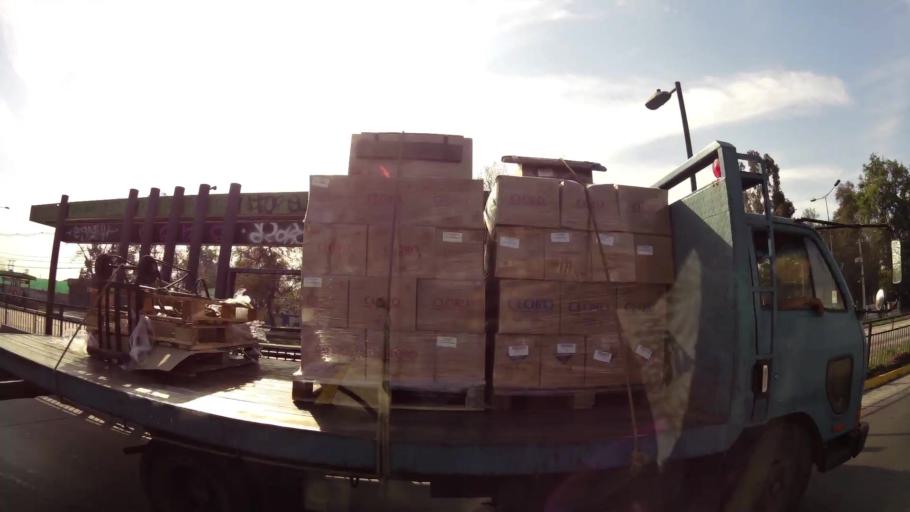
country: CL
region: Santiago Metropolitan
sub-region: Provincia de Santiago
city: La Pintana
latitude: -33.5611
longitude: -70.6307
